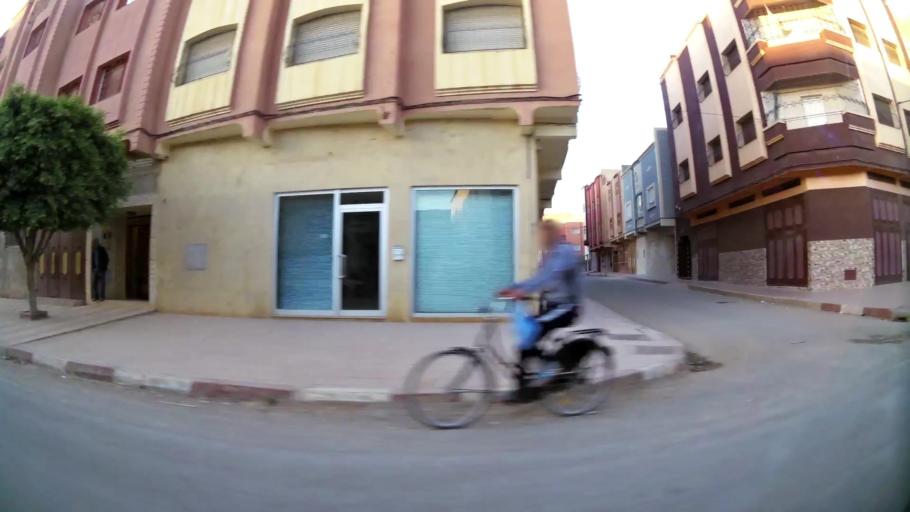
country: MA
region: Oriental
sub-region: Berkane-Taourirt
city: Berkane
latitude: 34.9137
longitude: -2.3199
